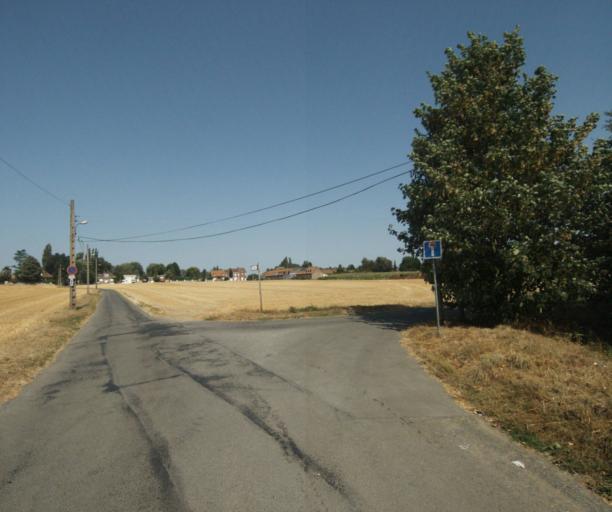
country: BE
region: Wallonia
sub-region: Province du Hainaut
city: Estaimpuis
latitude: 50.7060
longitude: 3.2483
